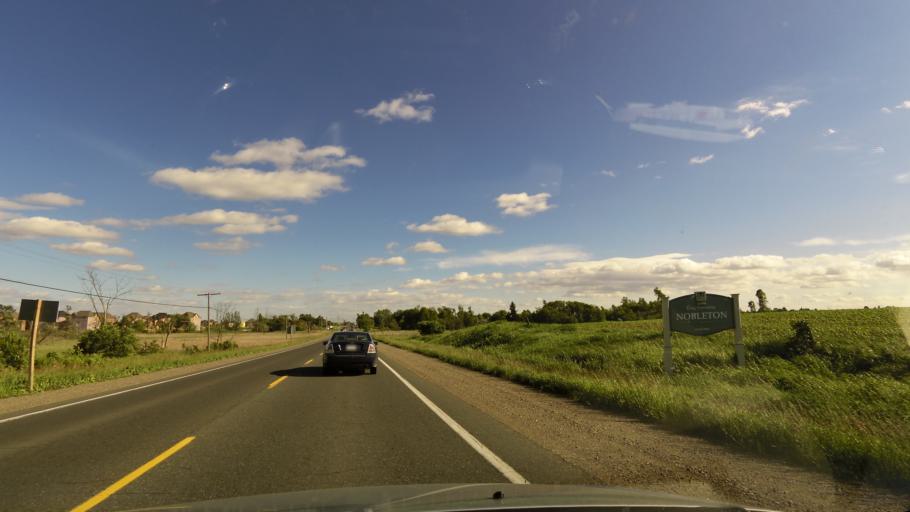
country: CA
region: Ontario
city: Vaughan
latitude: 43.9180
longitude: -79.6565
